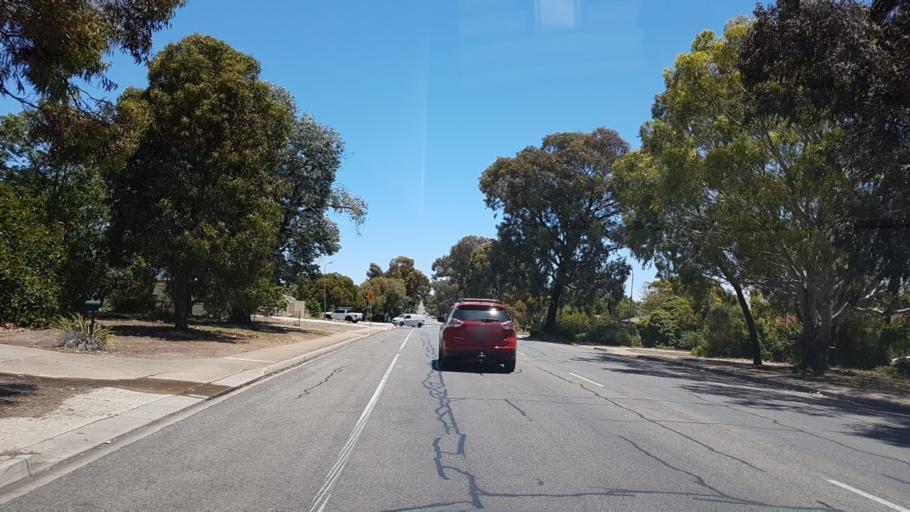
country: AU
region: South Australia
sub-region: Marion
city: Trott Park
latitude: -35.0931
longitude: 138.5563
